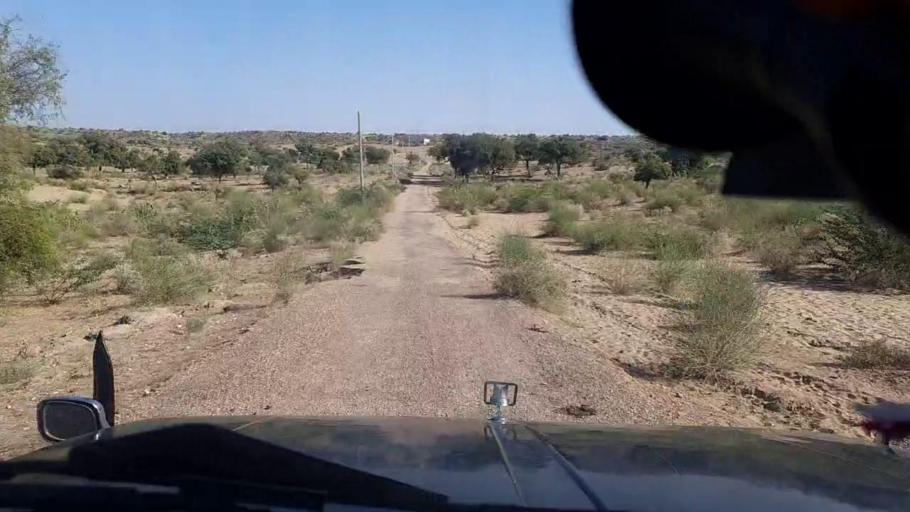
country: PK
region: Sindh
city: Diplo
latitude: 24.4700
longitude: 69.8055
